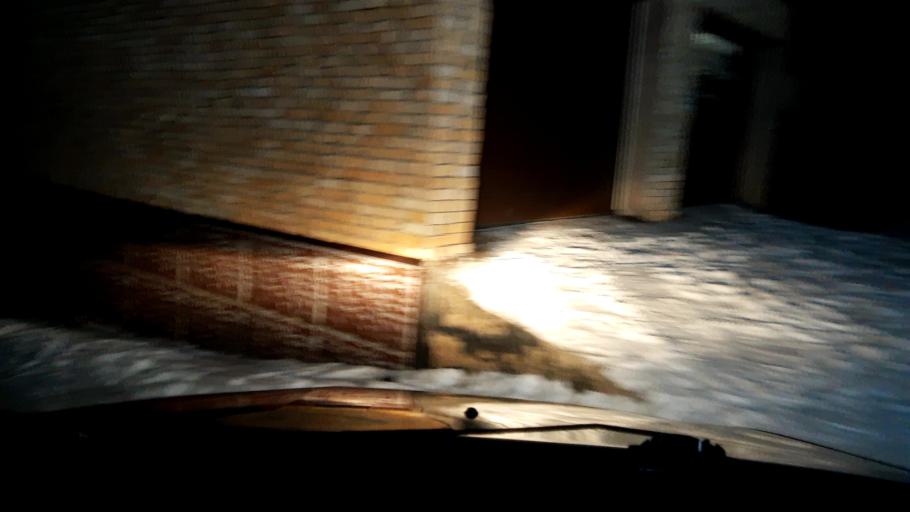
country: RU
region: Bashkortostan
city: Mikhaylovka
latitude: 54.8137
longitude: 55.8988
